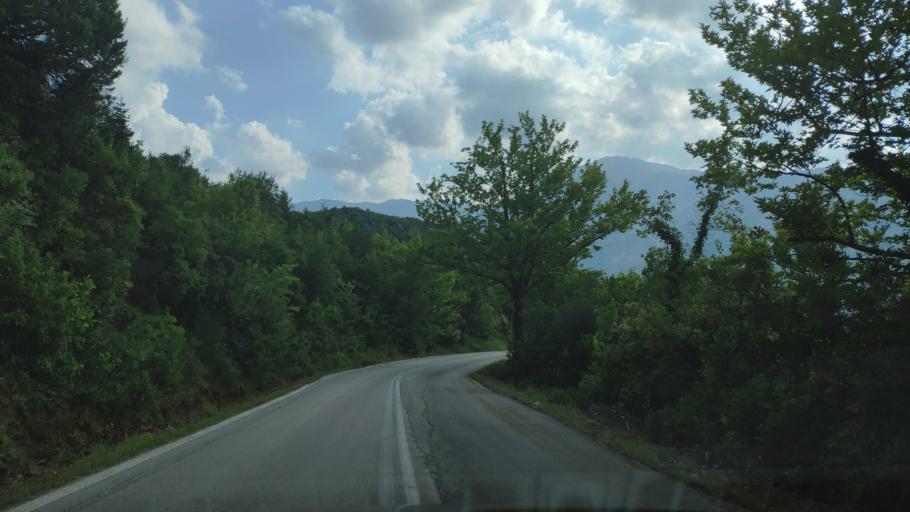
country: GR
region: Epirus
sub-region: Nomos Artas
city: Agios Dimitrios
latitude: 39.4588
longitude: 21.0580
